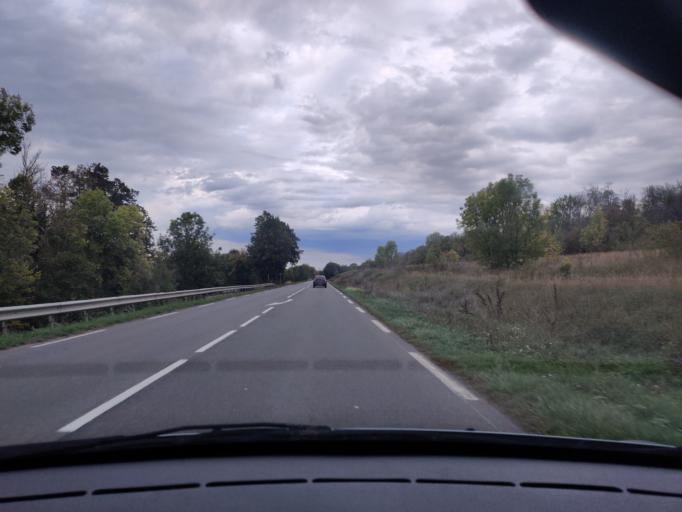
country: FR
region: Auvergne
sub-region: Departement du Puy-de-Dome
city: Saint-Bonnet-pres-Riom
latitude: 45.9173
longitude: 3.1225
